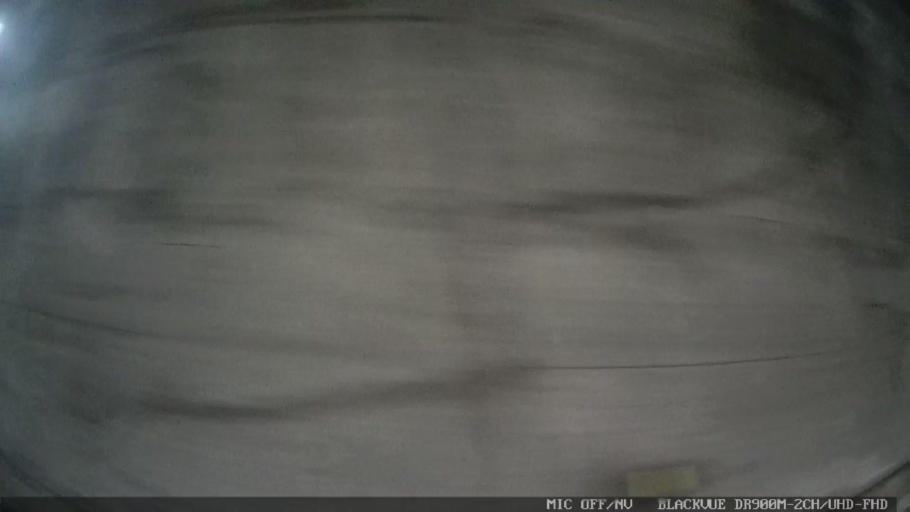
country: BR
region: Sao Paulo
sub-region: Cubatao
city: Cubatao
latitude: -23.8820
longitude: -46.4901
